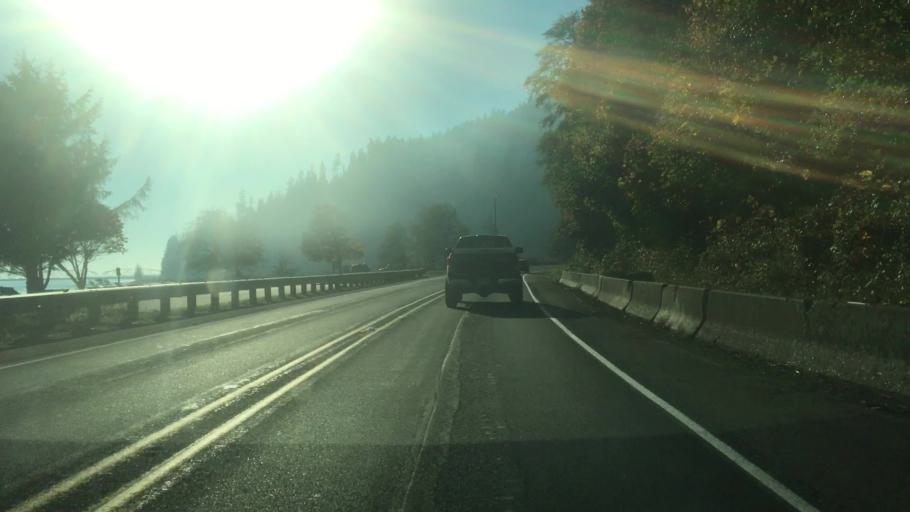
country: US
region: Oregon
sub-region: Clatsop County
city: Astoria
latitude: 46.2495
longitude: -123.8604
